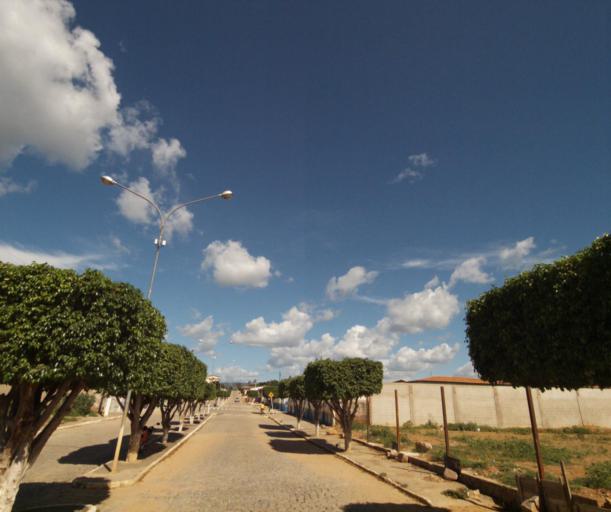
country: BR
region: Bahia
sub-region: Pocoes
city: Pocoes
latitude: -14.2413
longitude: -40.7697
